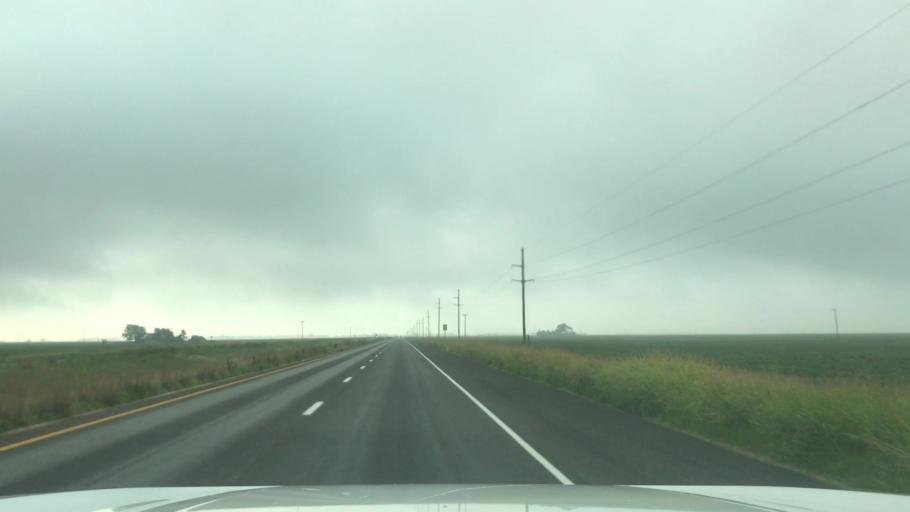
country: US
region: Texas
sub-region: Lubbock County
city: Slaton
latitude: 33.3766
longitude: -101.5802
